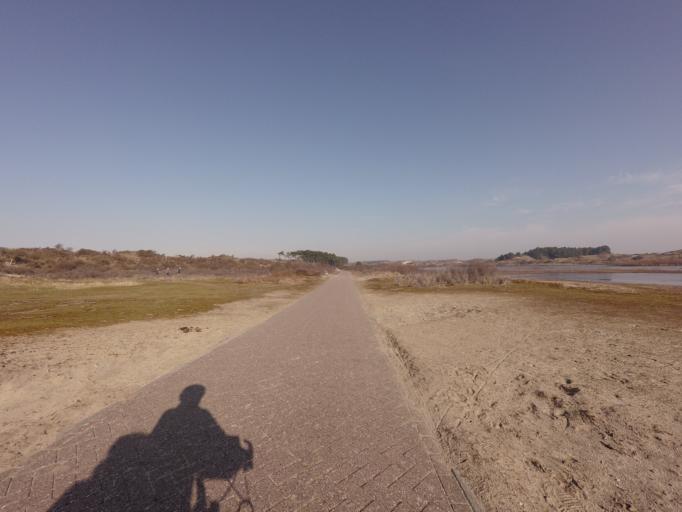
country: NL
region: North Holland
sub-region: Gemeente Zandvoort
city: Zandvoort
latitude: 52.4134
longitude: 4.5675
